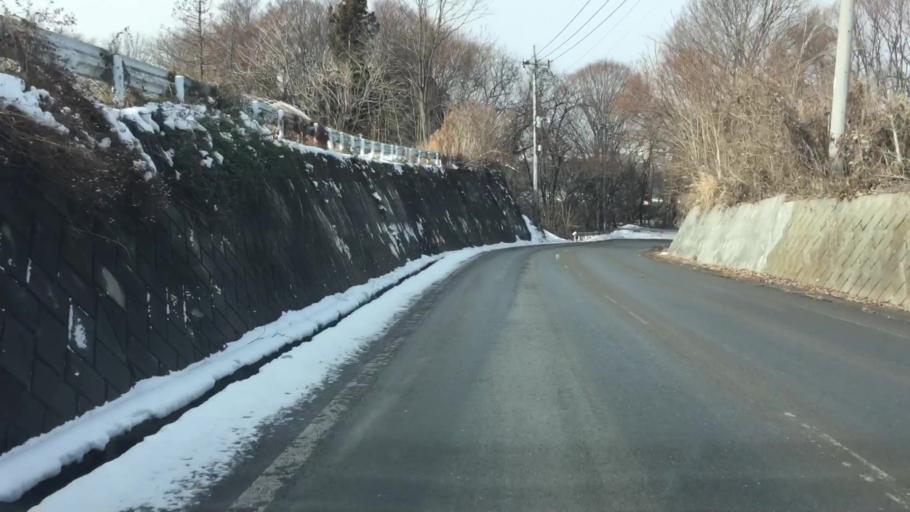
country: JP
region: Gunma
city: Numata
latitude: 36.6378
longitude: 139.0808
